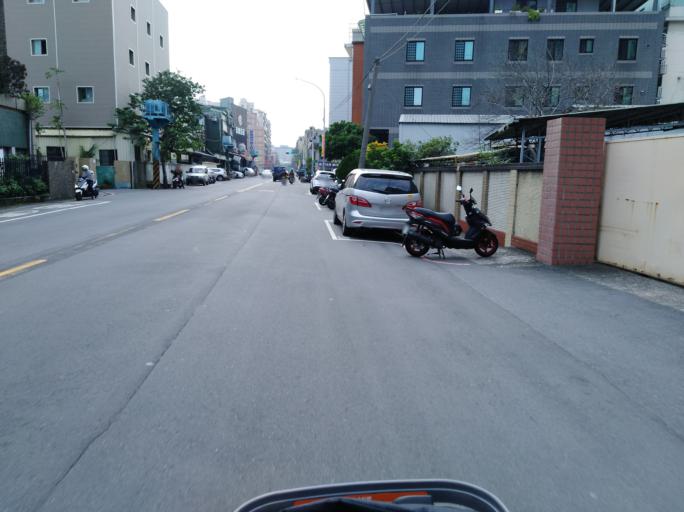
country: TW
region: Taipei
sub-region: Taipei
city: Banqiao
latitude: 25.0281
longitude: 121.4321
